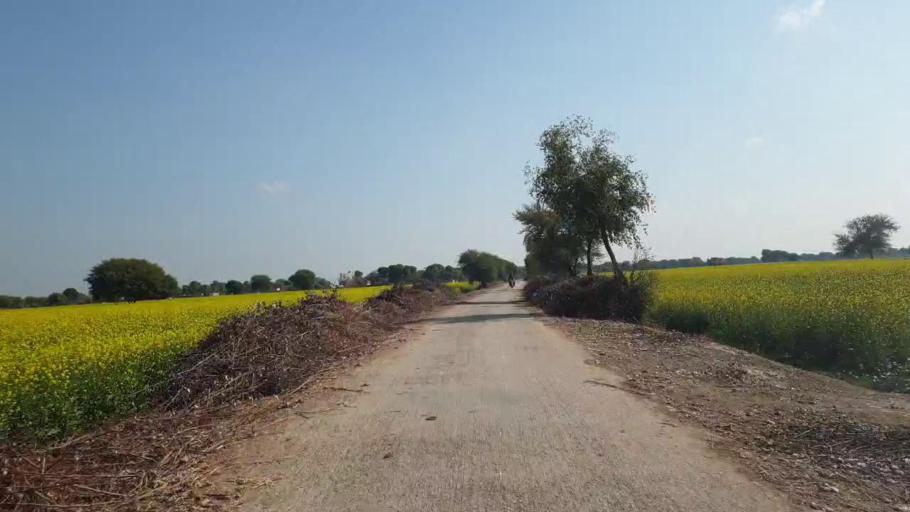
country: PK
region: Sindh
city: Shahpur Chakar
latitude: 26.0568
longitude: 68.5945
